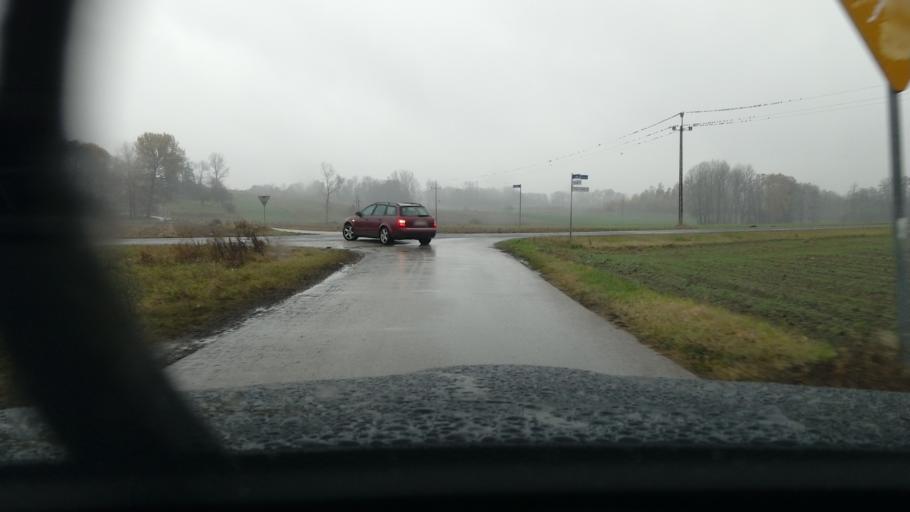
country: PL
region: Lodz Voivodeship
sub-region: Powiat skierniewicki
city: Godzianow
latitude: 51.9001
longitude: 20.0512
